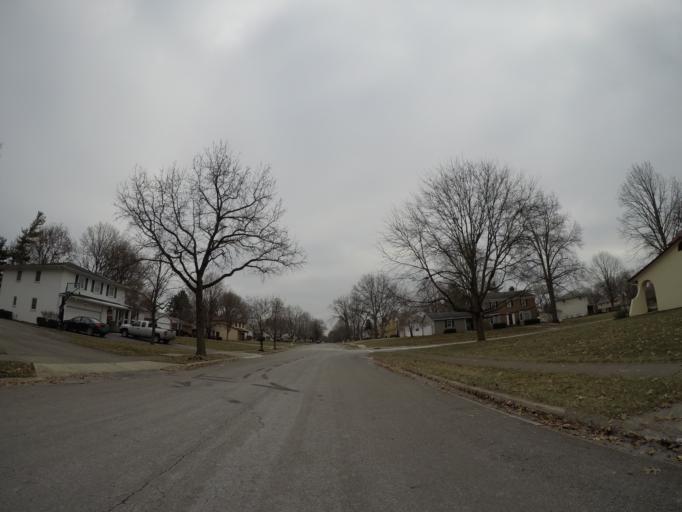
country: US
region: Ohio
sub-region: Franklin County
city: Upper Arlington
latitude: 40.0489
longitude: -83.0579
